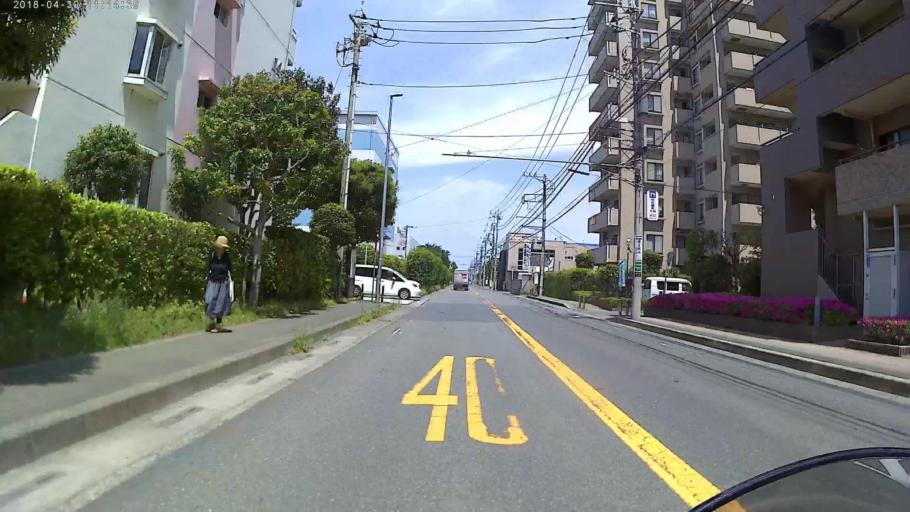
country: JP
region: Kanagawa
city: Minami-rinkan
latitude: 35.4755
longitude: 139.4315
